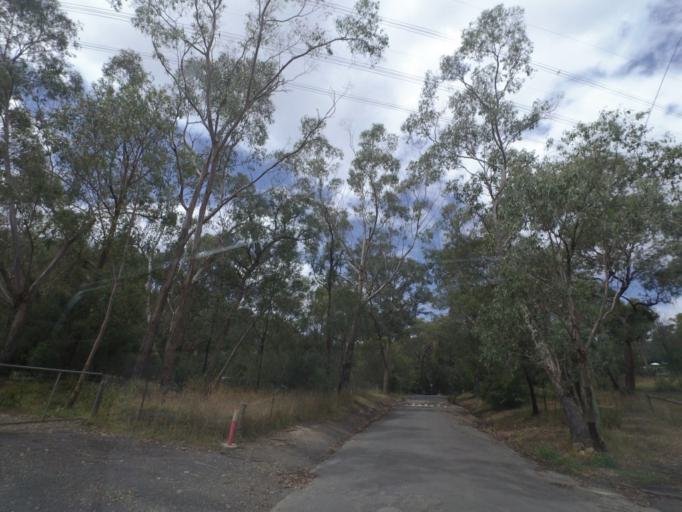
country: AU
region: Victoria
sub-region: Manningham
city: Park Orchards
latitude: -37.7921
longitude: 145.2089
